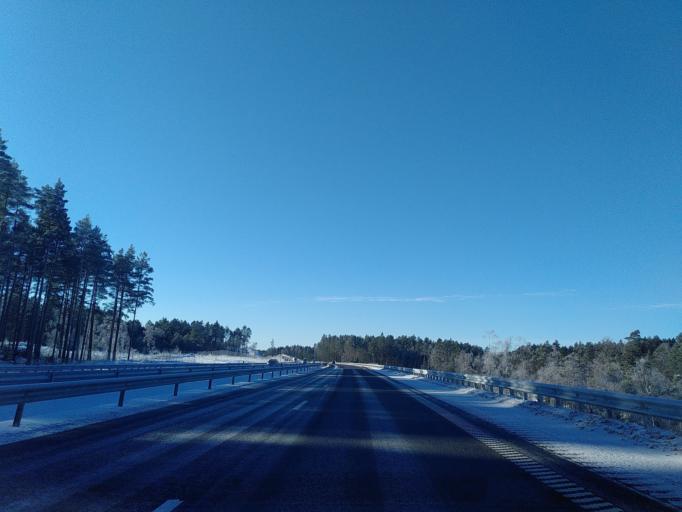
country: SE
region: Vaestra Goetaland
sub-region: Vargarda Kommun
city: Jonstorp
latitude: 57.9912
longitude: 12.7268
